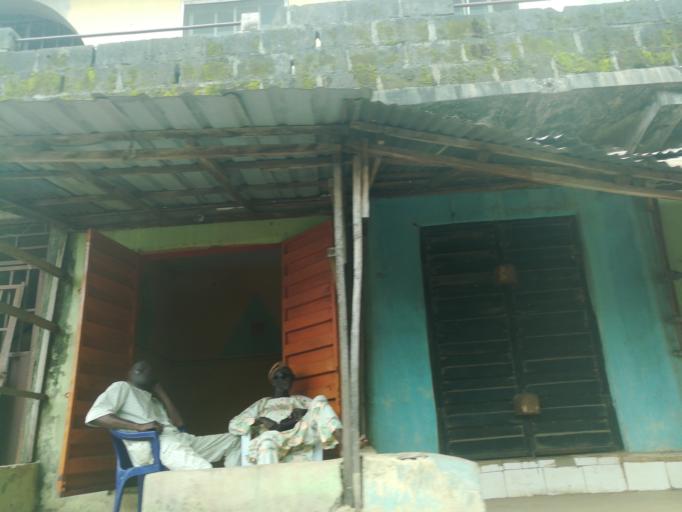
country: NG
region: Lagos
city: Ikorodu
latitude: 6.6138
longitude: 3.5071
